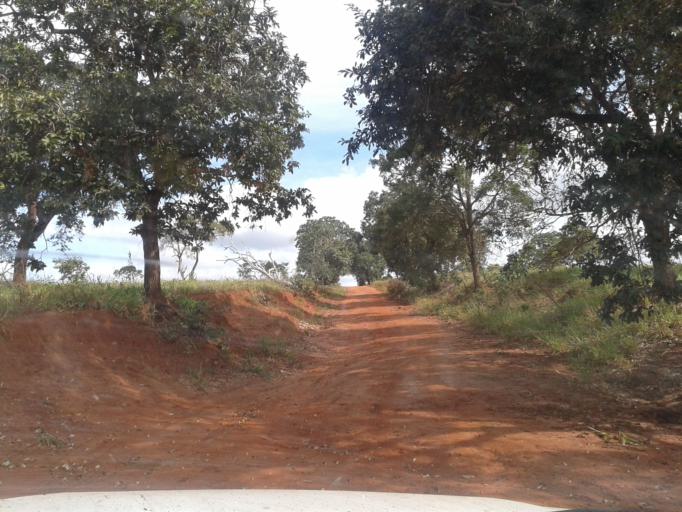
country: BR
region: Minas Gerais
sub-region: Campina Verde
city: Campina Verde
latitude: -19.4297
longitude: -49.7189
